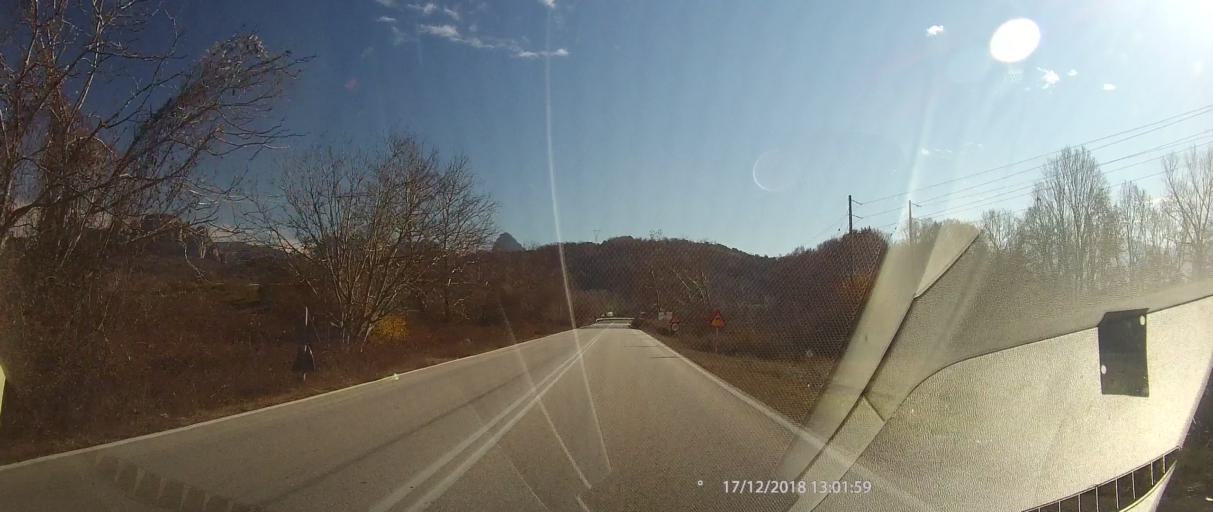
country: GR
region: Thessaly
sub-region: Trikala
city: Kastraki
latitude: 39.7290
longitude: 21.5909
